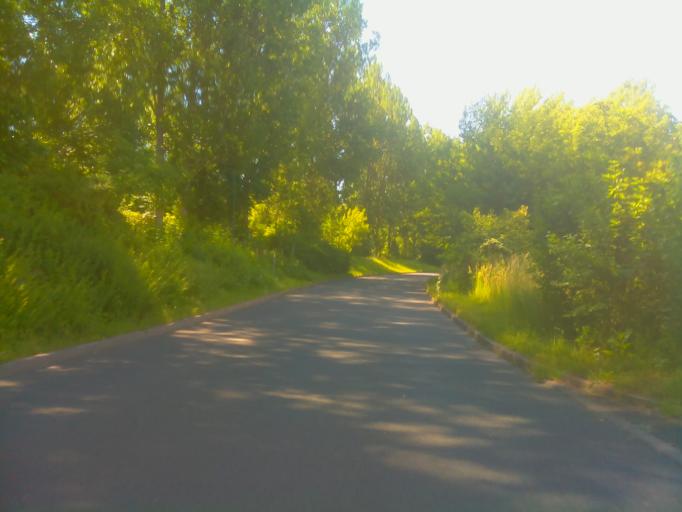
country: DE
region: Thuringia
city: Rudolstadt
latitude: 50.6929
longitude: 11.3368
